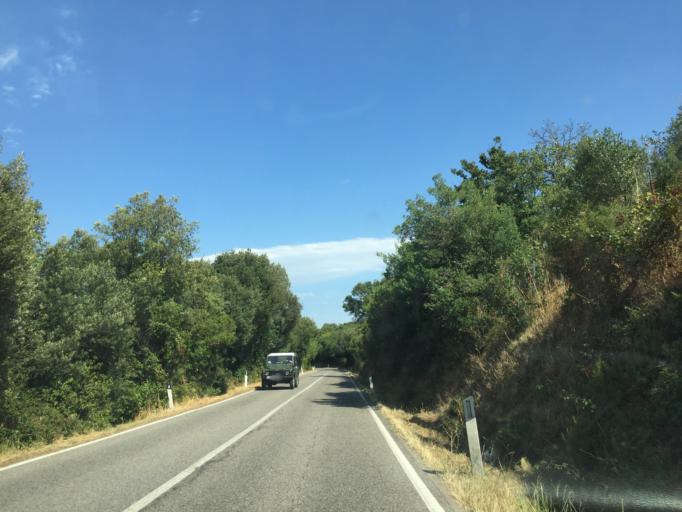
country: IT
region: Sardinia
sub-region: Provincia di Olbia-Tempio
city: Aggius
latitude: 40.9234
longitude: 9.0660
